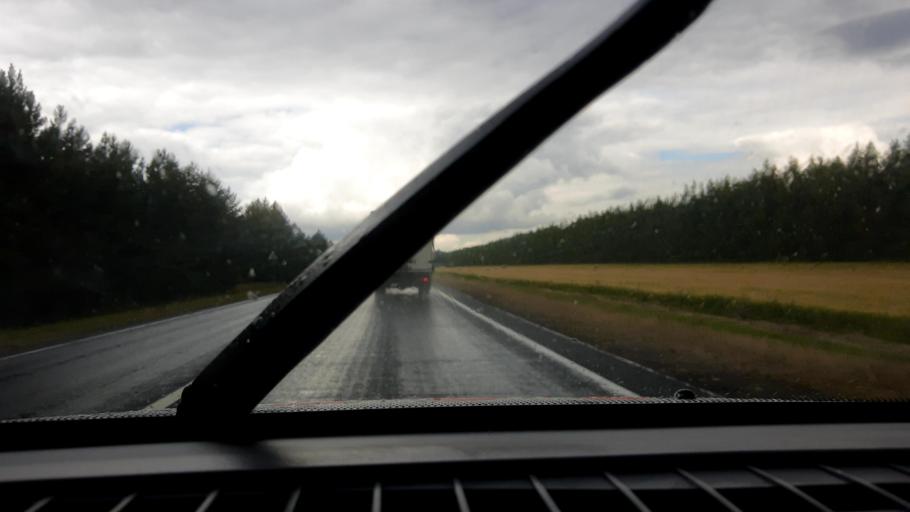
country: RU
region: Nizjnij Novgorod
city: Bol'shoye Murashkino
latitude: 55.9058
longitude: 44.7085
